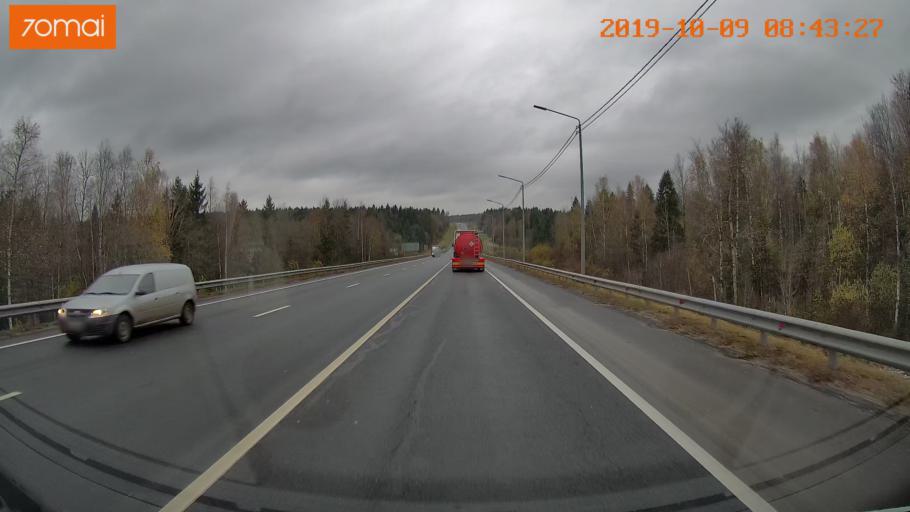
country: RU
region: Vologda
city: Gryazovets
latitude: 59.0242
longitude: 40.1143
